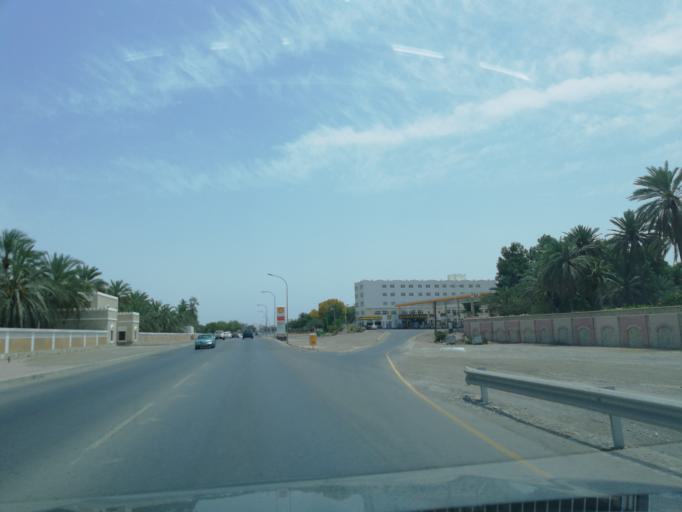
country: OM
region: Muhafazat Masqat
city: As Sib al Jadidah
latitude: 23.6795
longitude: 58.1675
